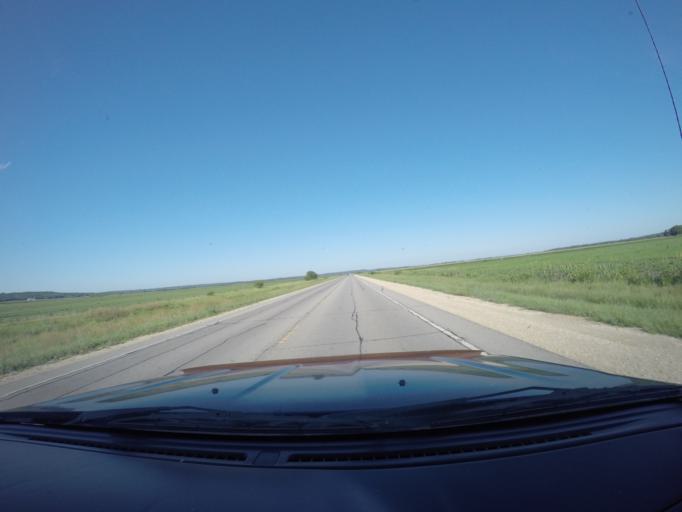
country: US
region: Kansas
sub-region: Jefferson County
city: Oskaloosa
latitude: 39.0872
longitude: -95.4556
